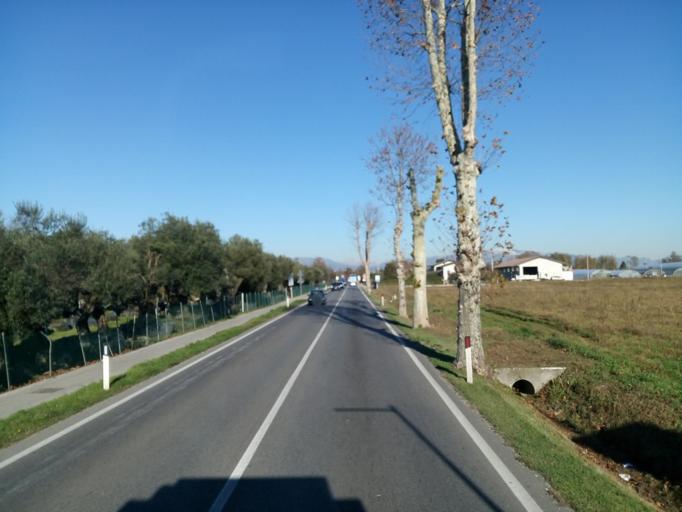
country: IT
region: Veneto
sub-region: Provincia di Treviso
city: Valla
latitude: 45.6918
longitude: 11.9276
